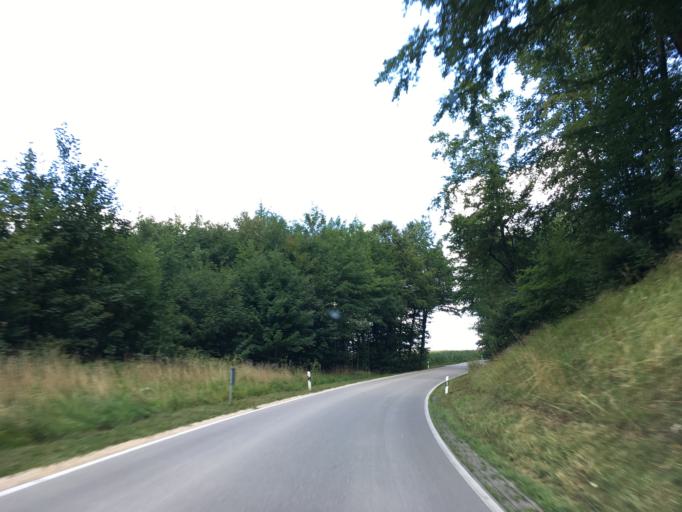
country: DE
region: Bavaria
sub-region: Upper Bavaria
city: Pittenhart
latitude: 47.9561
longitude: 12.3776
